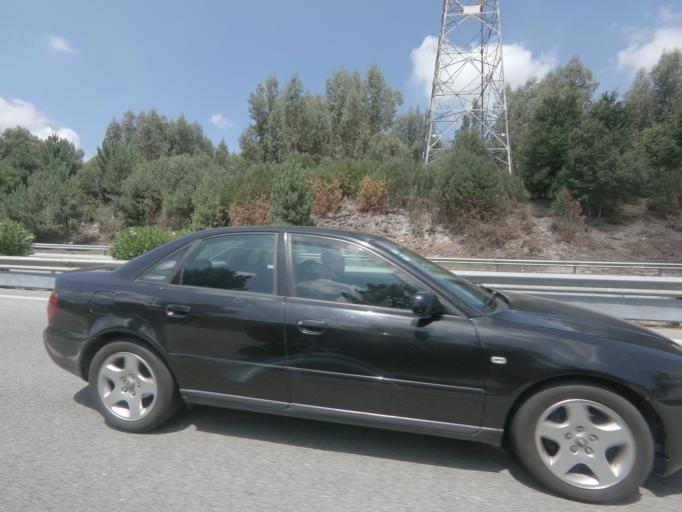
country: PT
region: Porto
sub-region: Paredes
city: Baltar
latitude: 41.1697
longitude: -8.3854
